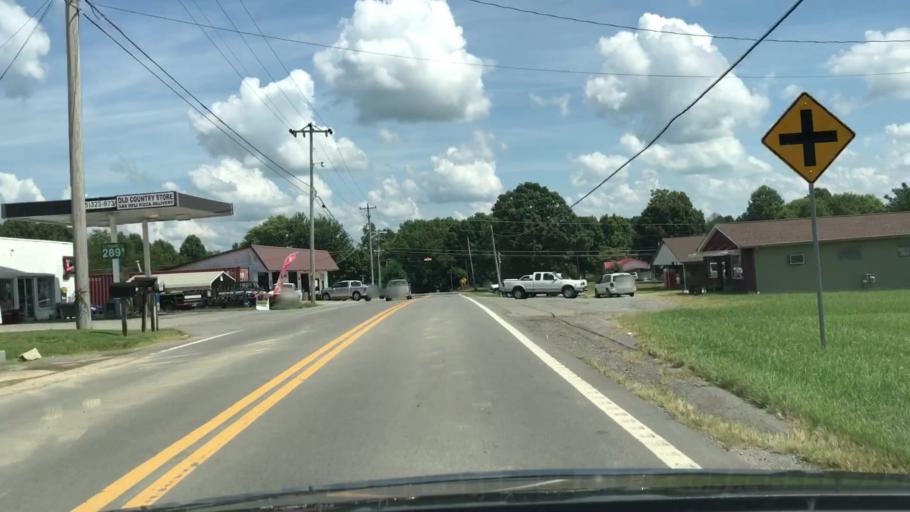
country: US
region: Tennessee
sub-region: Sumner County
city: Portland
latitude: 36.5178
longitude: -86.5634
